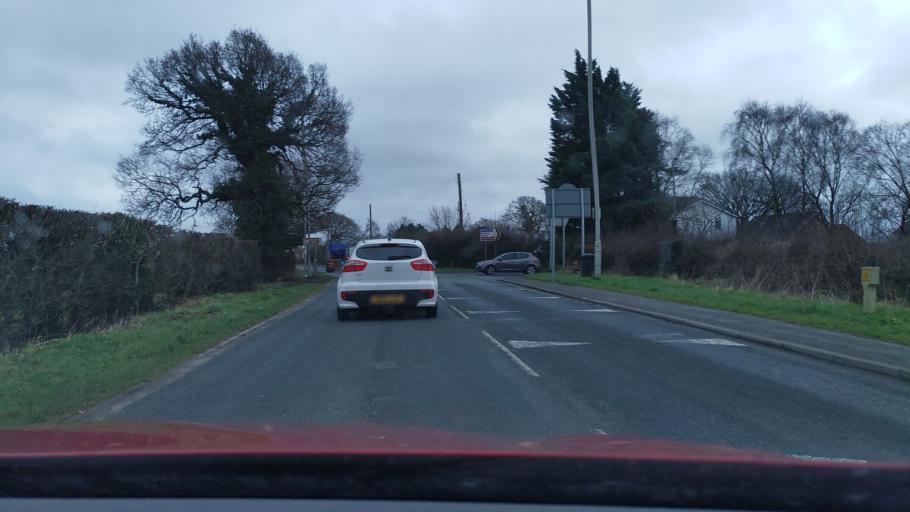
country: GB
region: England
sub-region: Lancashire
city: Croston
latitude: 53.6626
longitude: -2.7305
